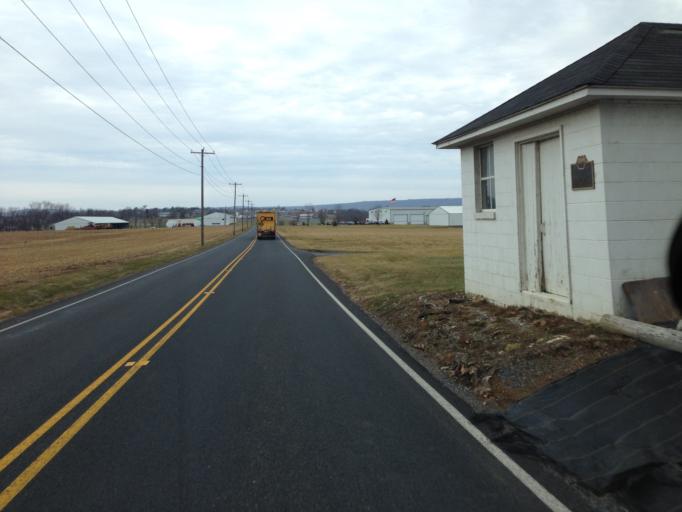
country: US
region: Pennsylvania
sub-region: Lancaster County
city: Manheim
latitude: 40.1619
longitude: -76.3663
